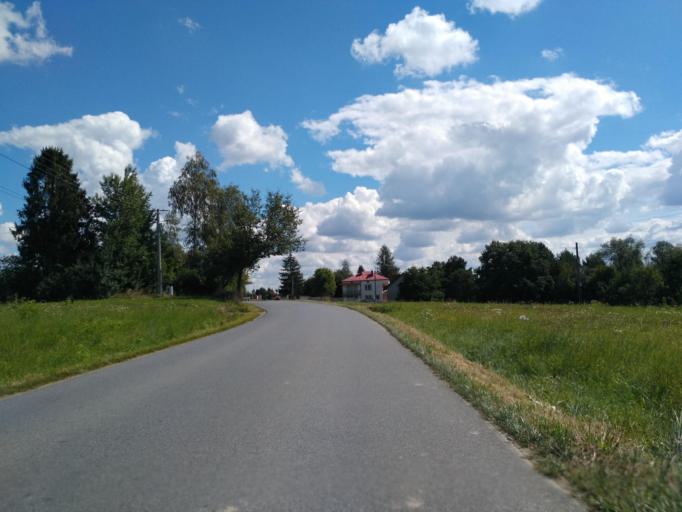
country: PL
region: Subcarpathian Voivodeship
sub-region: Powiat jasielski
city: Skolyszyn
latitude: 49.7811
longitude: 21.3584
